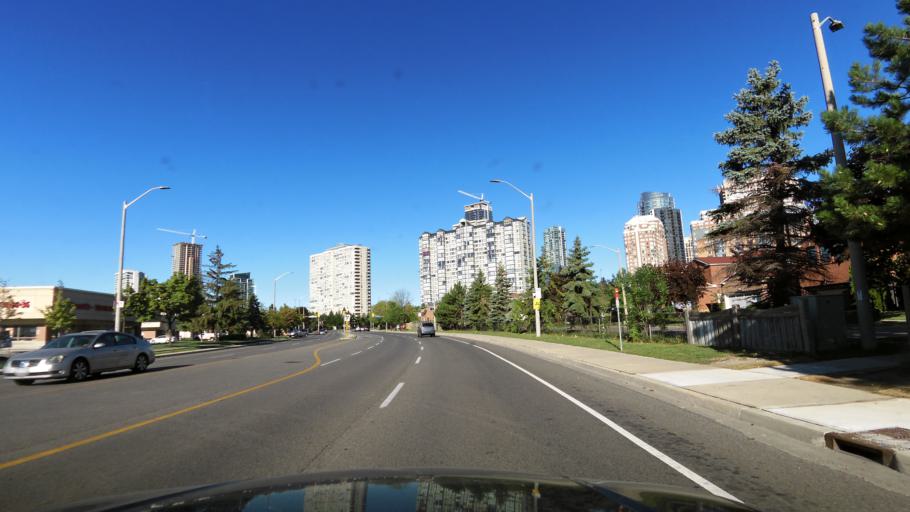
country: CA
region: Ontario
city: Mississauga
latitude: 43.5843
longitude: -79.6384
